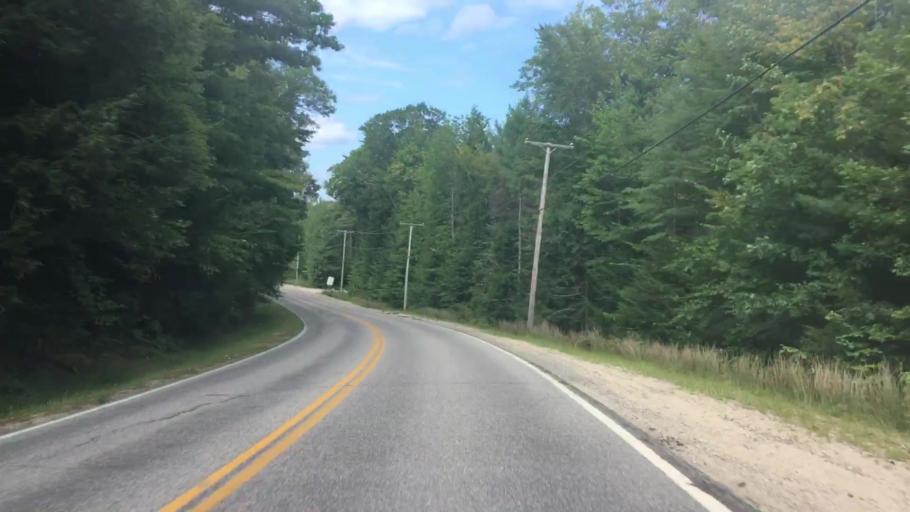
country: US
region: Maine
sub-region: Oxford County
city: Oxford
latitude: 44.0984
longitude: -70.5101
